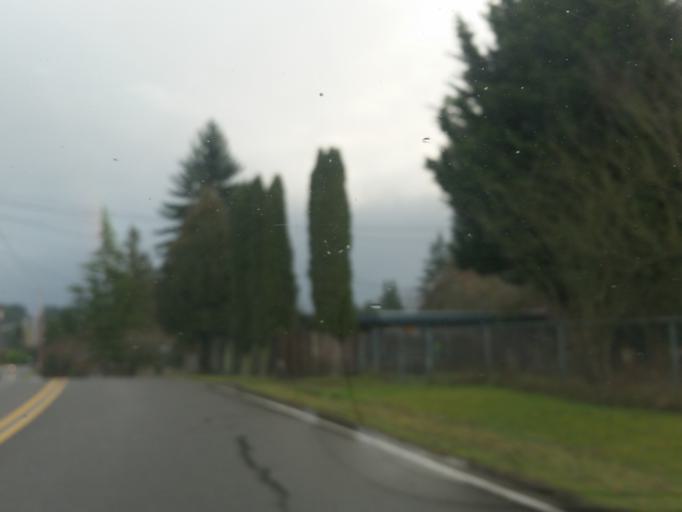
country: US
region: Washington
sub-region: Snohomish County
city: Brier
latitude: 47.7920
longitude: -122.2690
